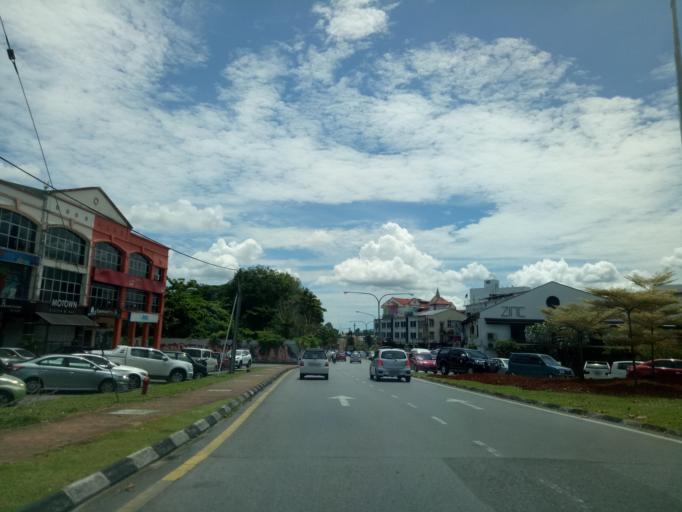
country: MY
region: Sarawak
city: Kuching
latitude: 1.5530
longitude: 110.3486
